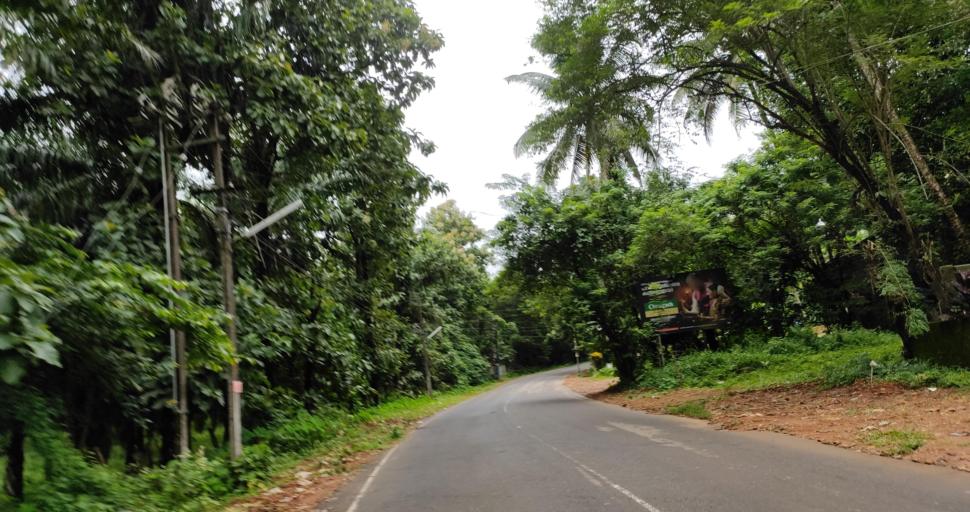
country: IN
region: Kerala
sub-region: Ernakulam
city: Angamali
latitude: 10.2907
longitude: 76.5023
